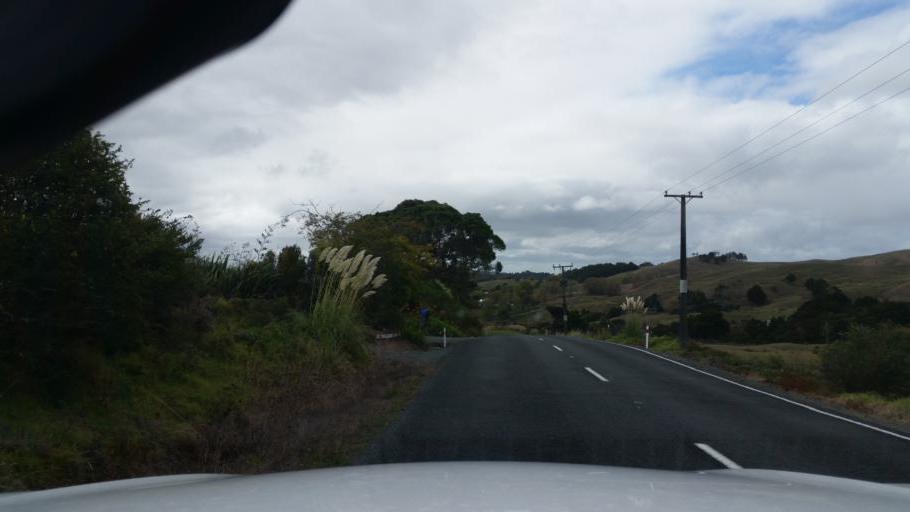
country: NZ
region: Auckland
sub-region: Auckland
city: Wellsford
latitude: -36.1379
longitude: 174.3214
